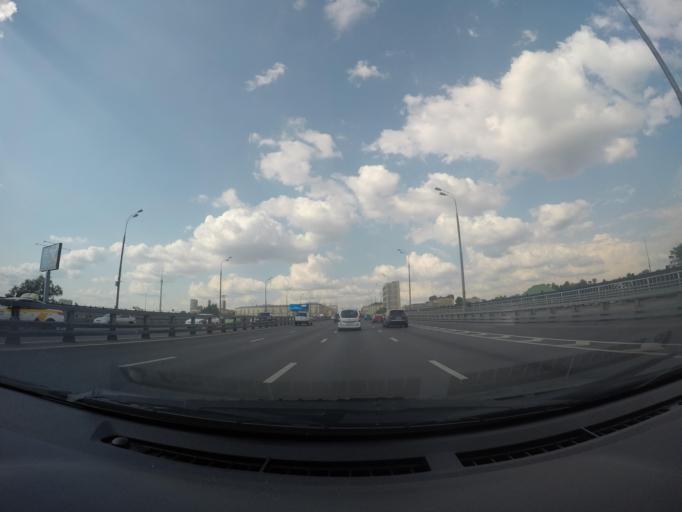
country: RU
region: Moscow
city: Mar'ina Roshcha
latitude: 55.7966
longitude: 37.6349
